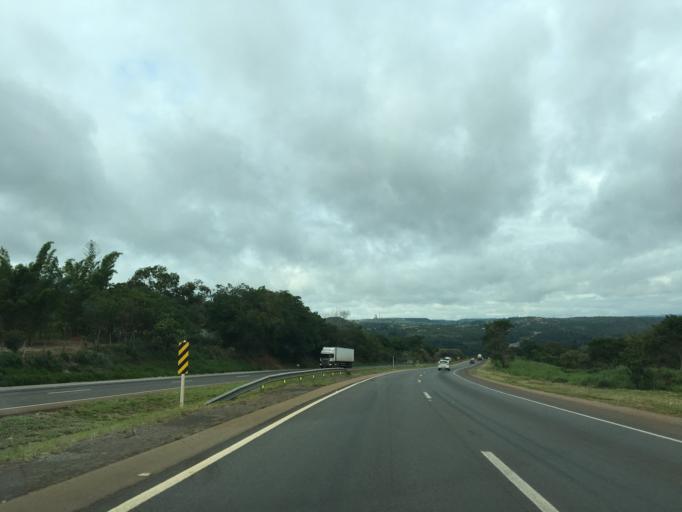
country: BR
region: Goias
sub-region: Abadiania
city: Abadiania
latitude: -16.1145
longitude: -48.3341
